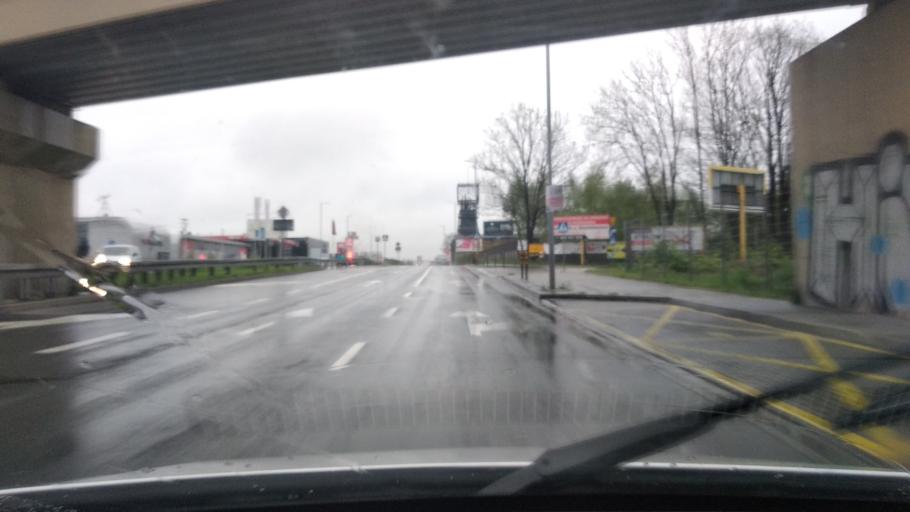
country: PL
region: Silesian Voivodeship
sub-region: Katowice
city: Katowice
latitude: 50.2579
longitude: 18.9851
